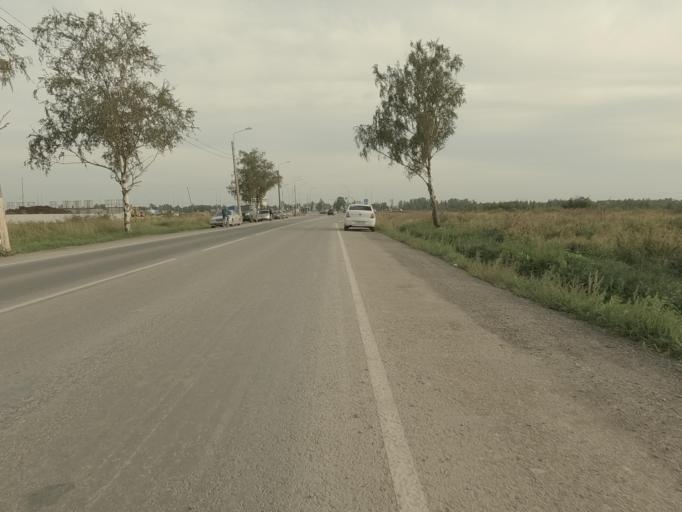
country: RU
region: St.-Petersburg
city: Strel'na
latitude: 59.8429
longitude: 30.0911
